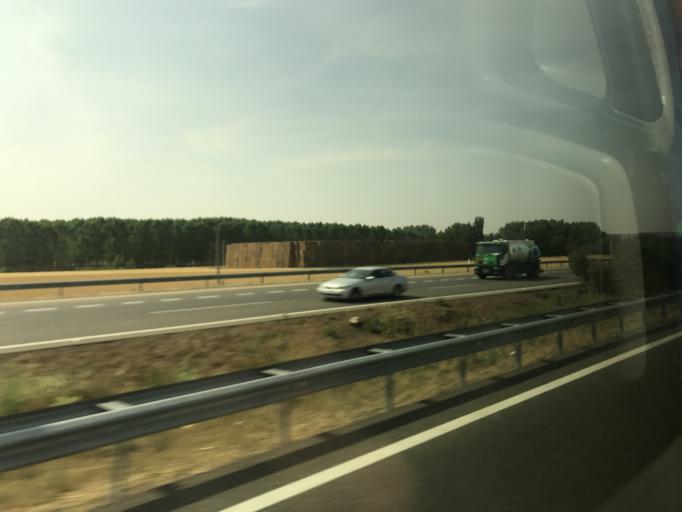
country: ES
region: Castille and Leon
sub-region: Provincia de Palencia
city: Villodrigo
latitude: 42.1561
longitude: -4.0825
